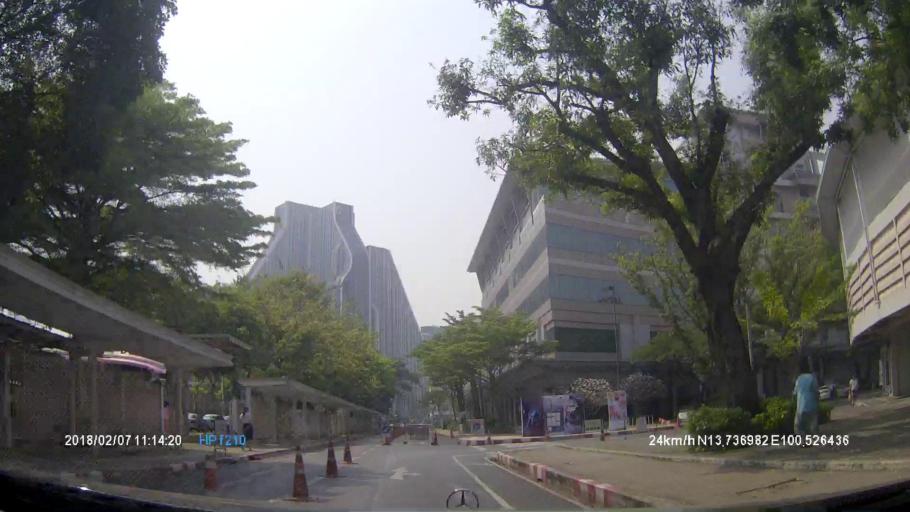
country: TH
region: Bangkok
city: Pathum Wan
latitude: 13.7369
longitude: 100.5264
